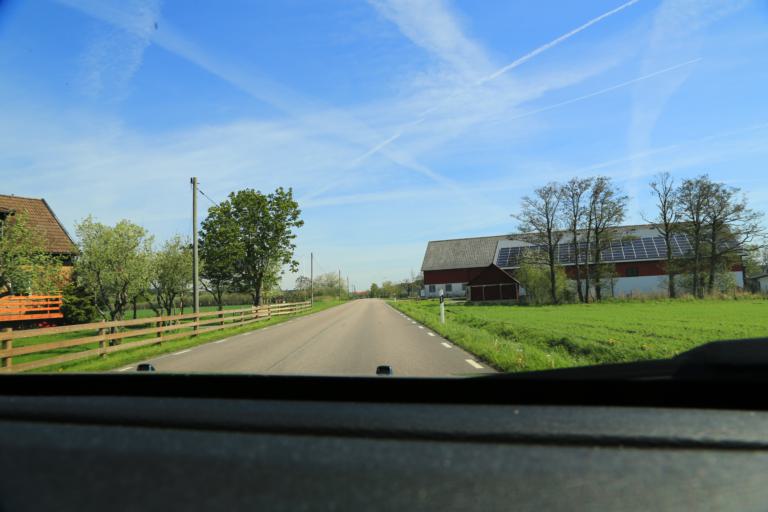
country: SE
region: Halland
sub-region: Varbergs Kommun
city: Varberg
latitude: 57.1567
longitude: 12.2732
